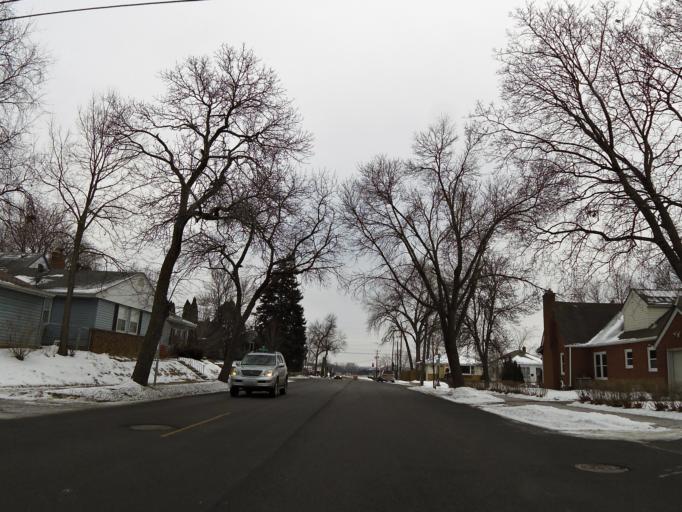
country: US
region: Minnesota
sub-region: Dakota County
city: Mendota Heights
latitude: 44.9195
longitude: -93.1925
